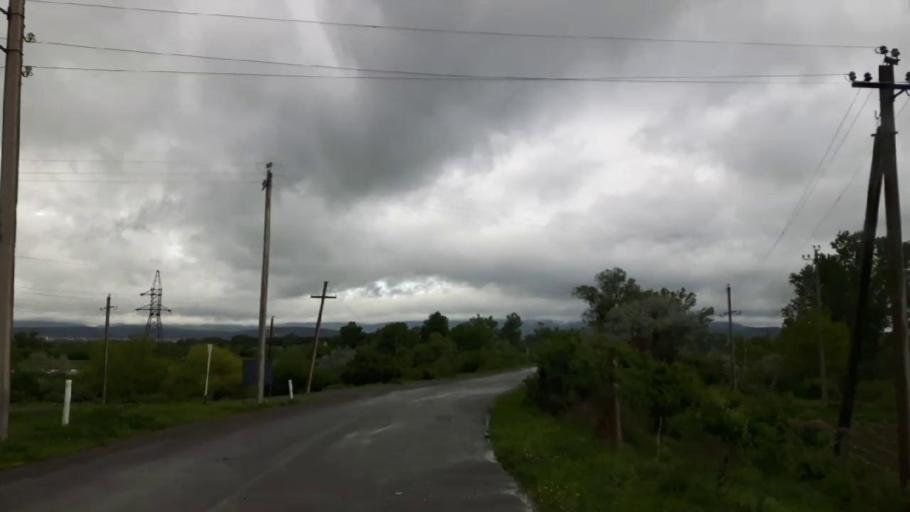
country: GE
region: Shida Kartli
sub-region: Khashuris Raioni
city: Khashuri
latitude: 41.9896
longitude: 43.6601
